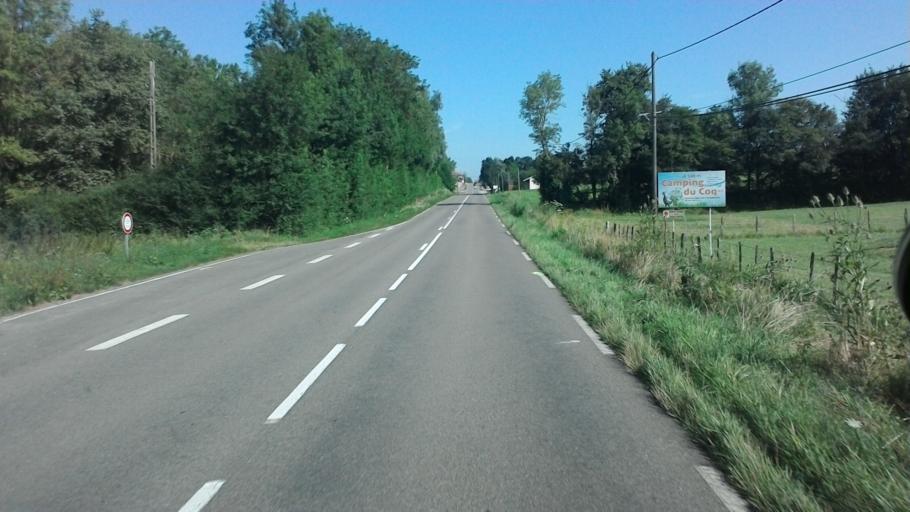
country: FR
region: Rhone-Alpes
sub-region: Departement de l'Ain
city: Saint-Trivier-de-Courtes
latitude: 46.4199
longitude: 5.1010
